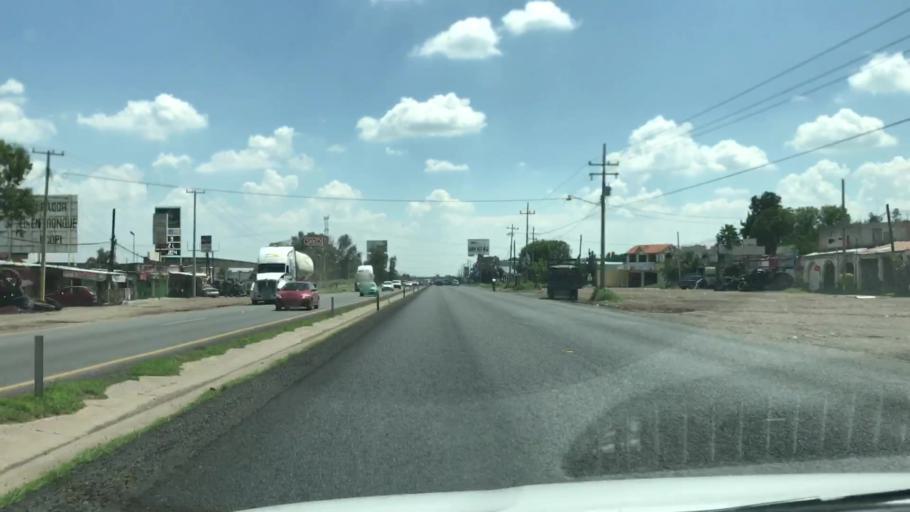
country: MX
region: Guanajuato
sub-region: Irapuato
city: San Jose de Bernalejo (El Guayabo)
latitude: 20.6318
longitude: -101.3896
